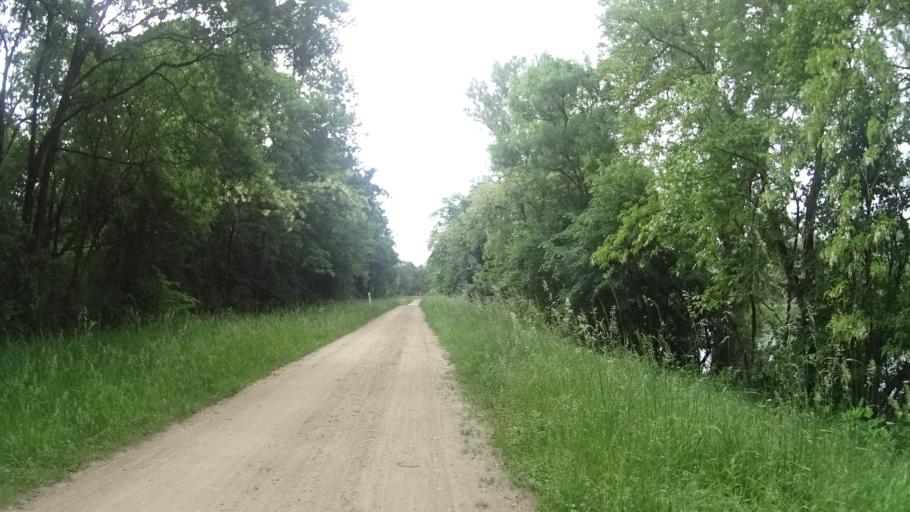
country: FR
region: Alsace
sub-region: Departement du Haut-Rhin
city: Kembs
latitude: 47.6912
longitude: 7.5168
